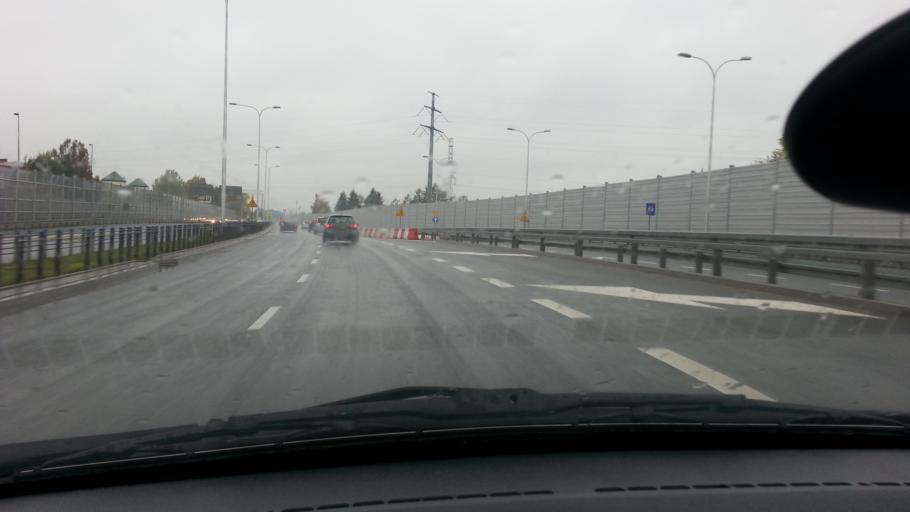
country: PL
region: Masovian Voivodeship
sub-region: Powiat pruszkowski
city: Michalowice
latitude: 52.1800
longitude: 20.8772
